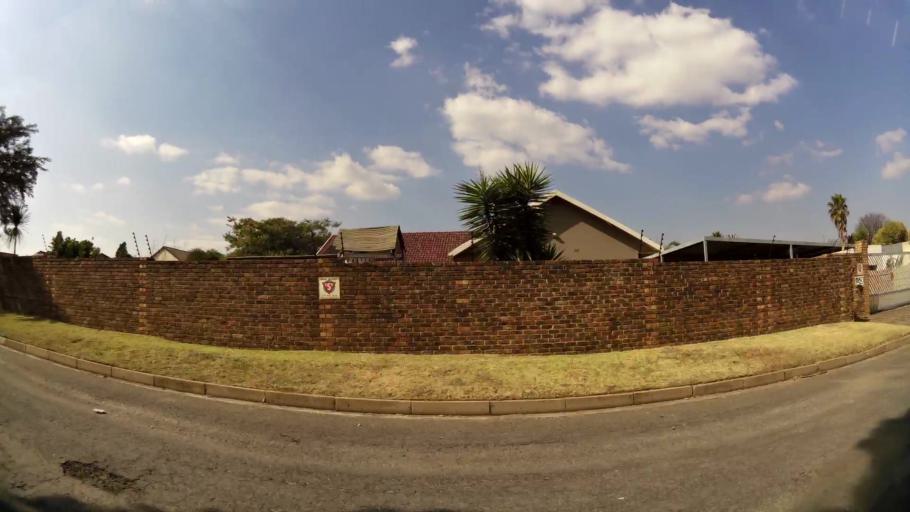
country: ZA
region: Gauteng
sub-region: City of Johannesburg Metropolitan Municipality
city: Modderfontein
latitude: -26.0858
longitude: 28.2272
